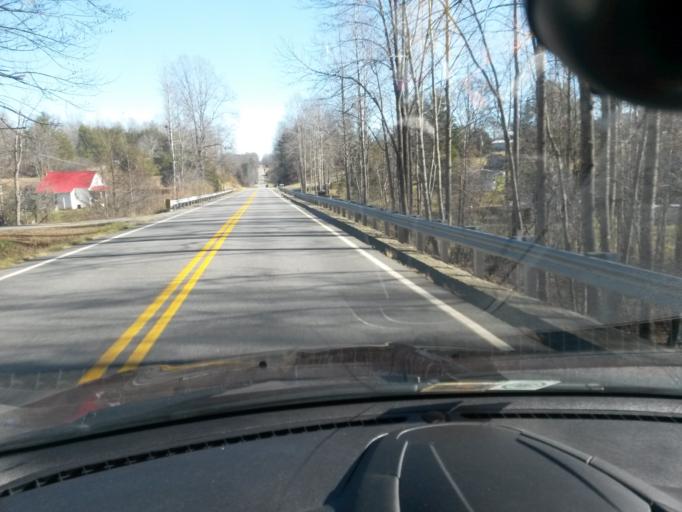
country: US
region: Virginia
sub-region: Patrick County
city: Patrick Springs
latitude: 36.7700
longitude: -80.1517
